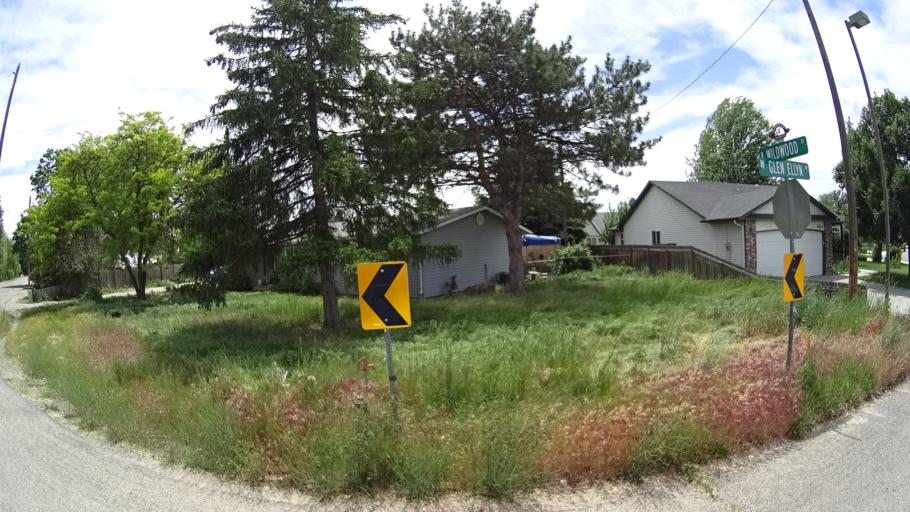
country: US
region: Idaho
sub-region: Ada County
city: Meridian
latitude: 43.6267
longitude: -116.3218
